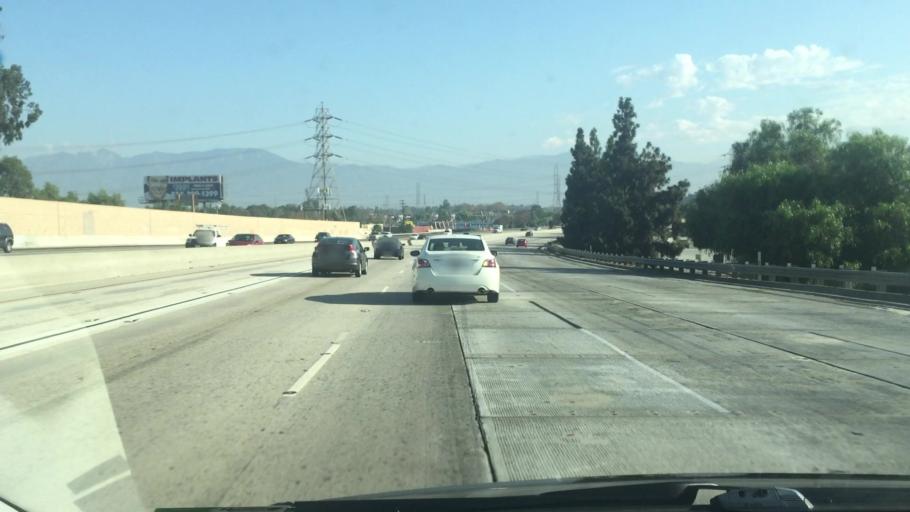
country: US
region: California
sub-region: Los Angeles County
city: West Whittier-Los Nietos
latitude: 34.0124
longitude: -118.0566
